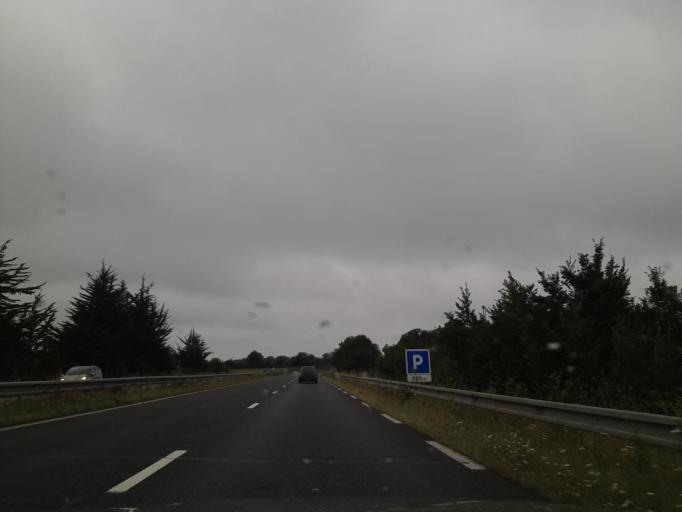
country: FR
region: Lower Normandy
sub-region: Departement de la Manche
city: Sainte-Mere-Eglise
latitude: 49.3684
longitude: -1.2864
